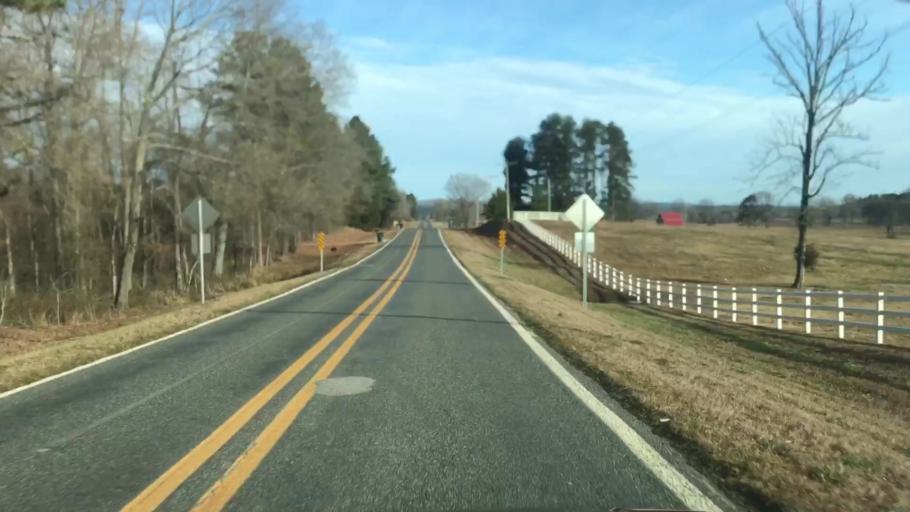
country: US
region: Arkansas
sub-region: Garland County
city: Rockwell
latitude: 34.4964
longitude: -93.2766
